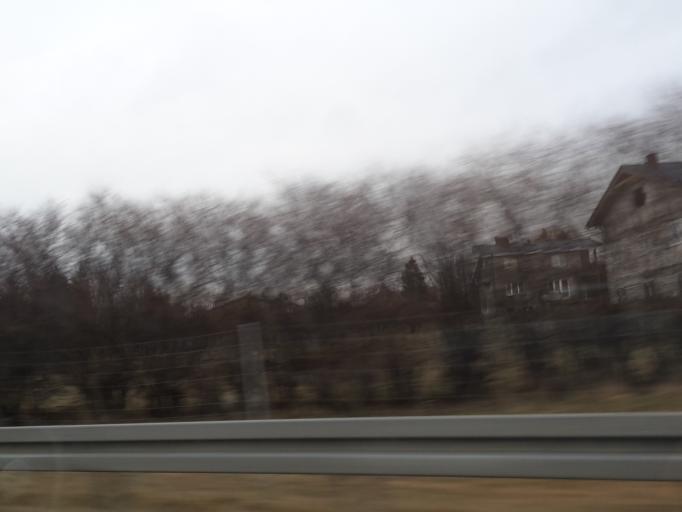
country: PL
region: Warmian-Masurian Voivodeship
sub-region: Powiat elblaski
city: Gronowo Gorne
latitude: 54.1352
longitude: 19.4546
